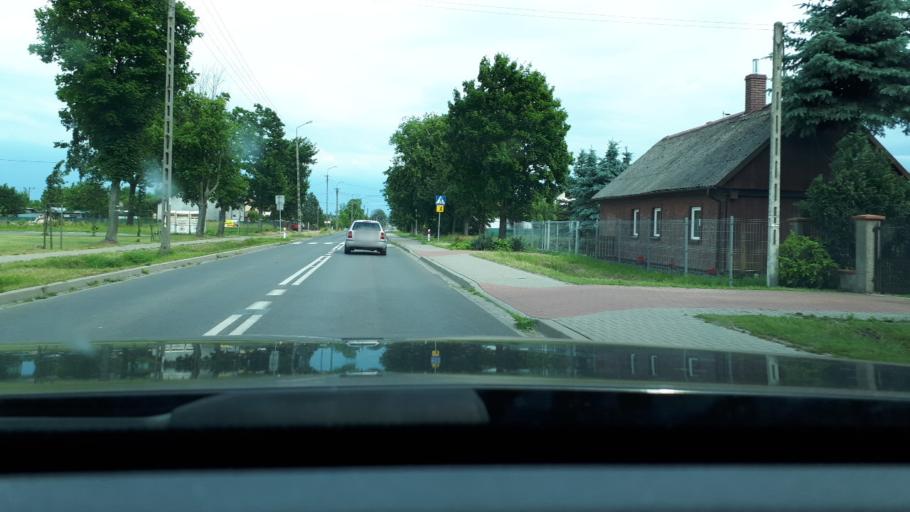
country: PL
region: Masovian Voivodeship
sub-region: Powiat warszawski zachodni
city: Kampinos
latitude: 52.2667
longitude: 20.4709
